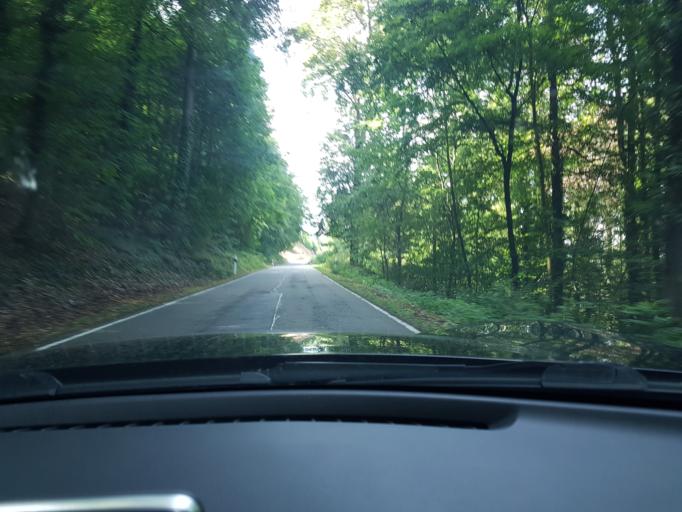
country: DE
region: Baden-Wuerttemberg
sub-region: Regierungsbezirk Stuttgart
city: Gundelsheim
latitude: 49.2791
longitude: 9.1379
